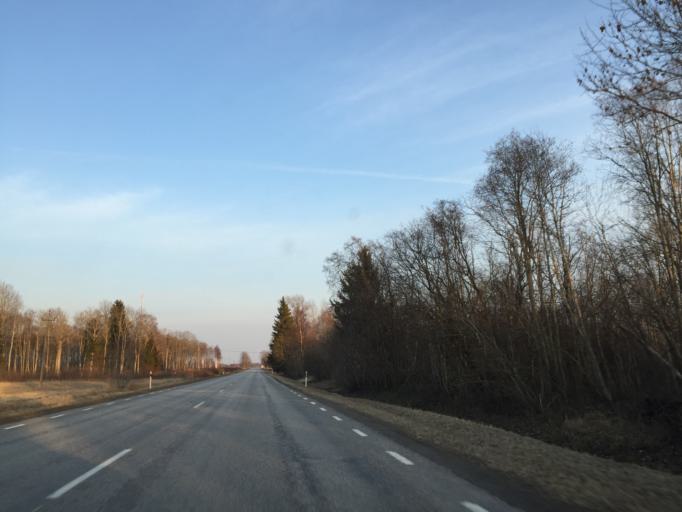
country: EE
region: Laeaene
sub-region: Lihula vald
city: Lihula
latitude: 58.5334
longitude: 24.0388
